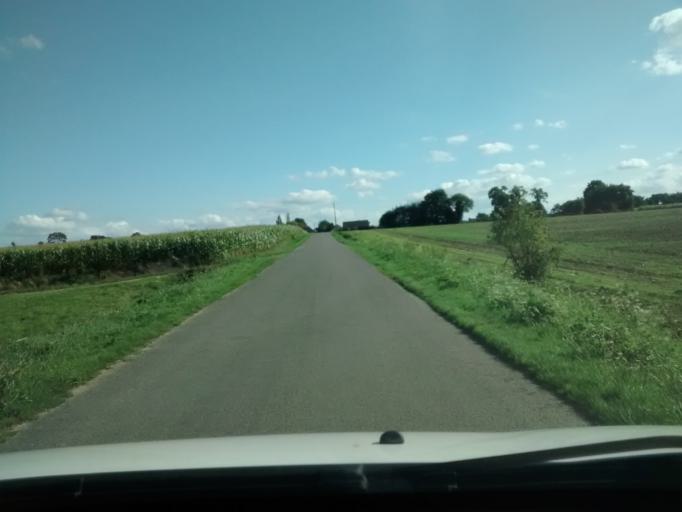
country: FR
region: Brittany
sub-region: Departement d'Ille-et-Vilaine
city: Chantepie
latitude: 48.0861
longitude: -1.5772
